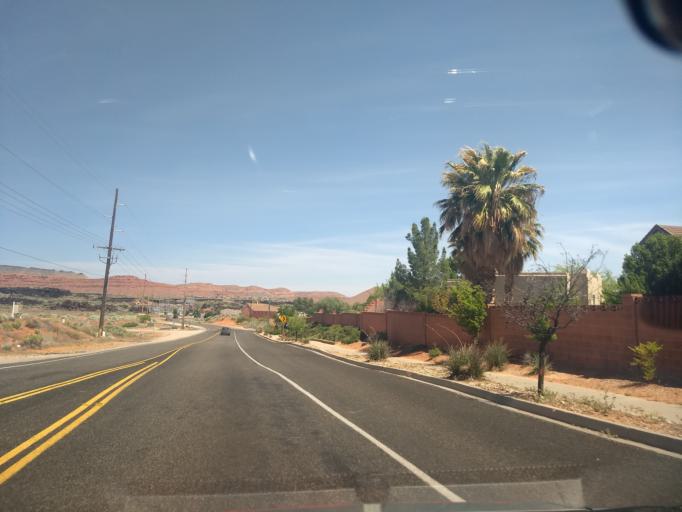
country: US
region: Utah
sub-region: Washington County
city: Santa Clara
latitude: 37.1465
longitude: -113.6581
